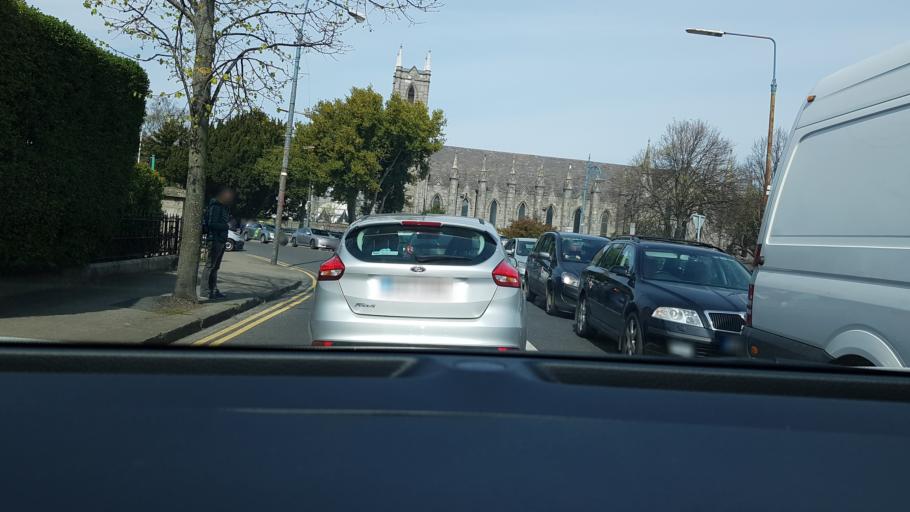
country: IE
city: Clonskeagh
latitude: 53.3240
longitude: -6.2303
